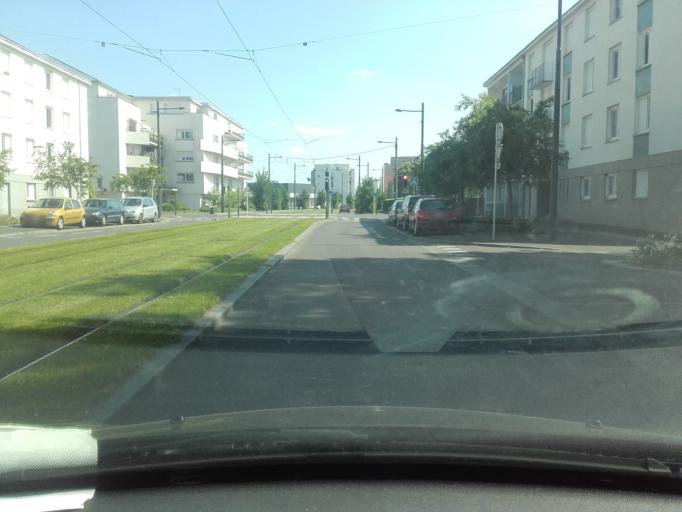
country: FR
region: Centre
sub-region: Departement d'Indre-et-Loire
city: Saint-Cyr-sur-Loire
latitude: 47.4205
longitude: 0.6837
